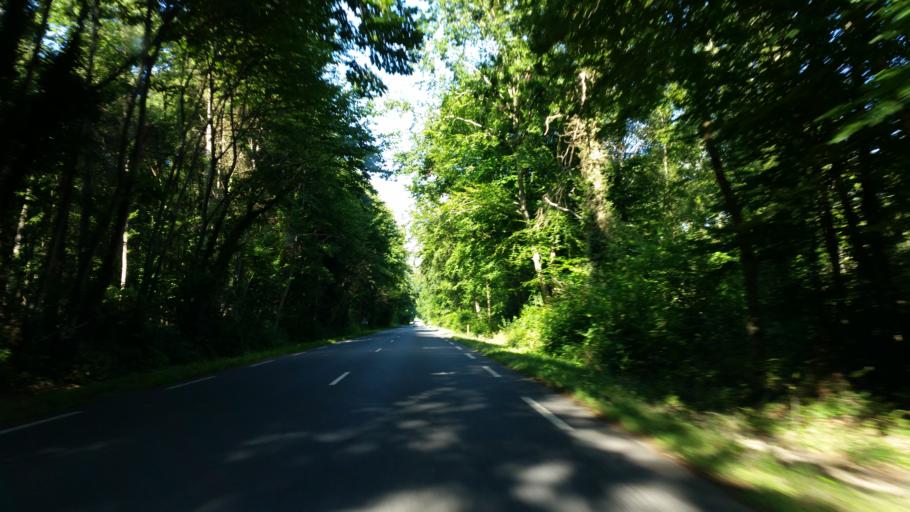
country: FR
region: Lower Normandy
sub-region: Departement du Calvados
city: Saint-Gatien-des-Bois
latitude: 49.3495
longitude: 0.1571
